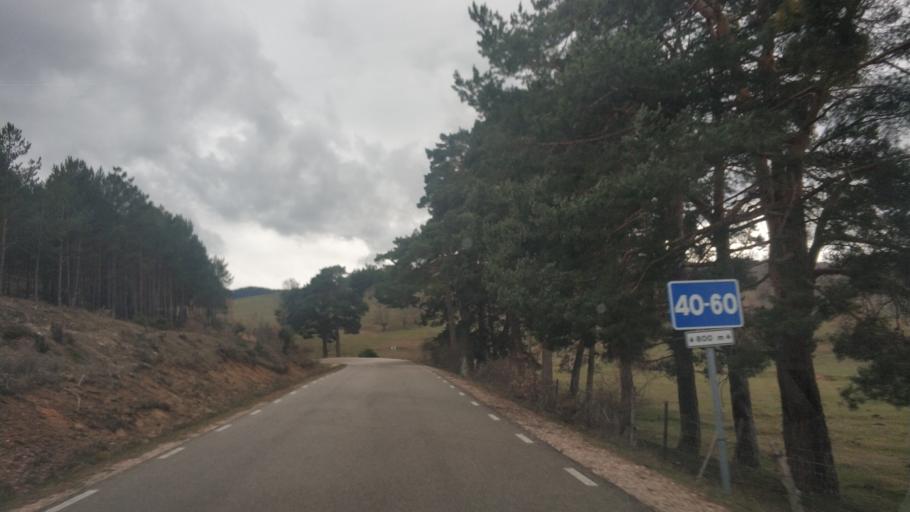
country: ES
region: Castille and Leon
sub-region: Provincia de Burgos
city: Canicosa de la Sierra
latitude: 41.9452
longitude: -3.0349
